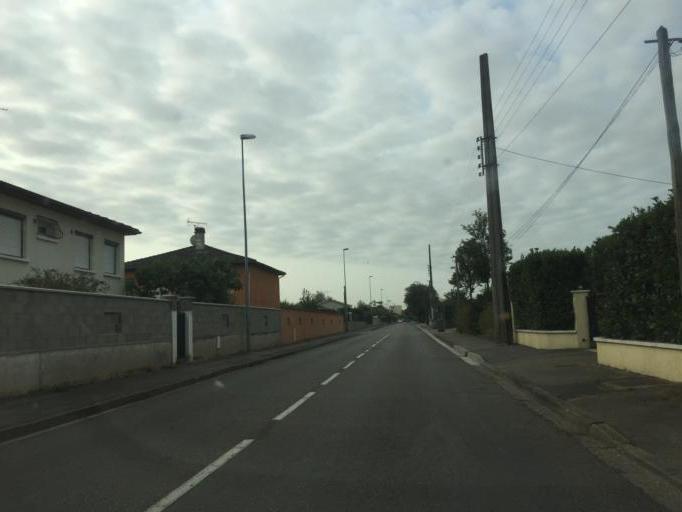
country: FR
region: Rhone-Alpes
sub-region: Departement du Rhone
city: Meyzieu
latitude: 45.7808
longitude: 5.0053
